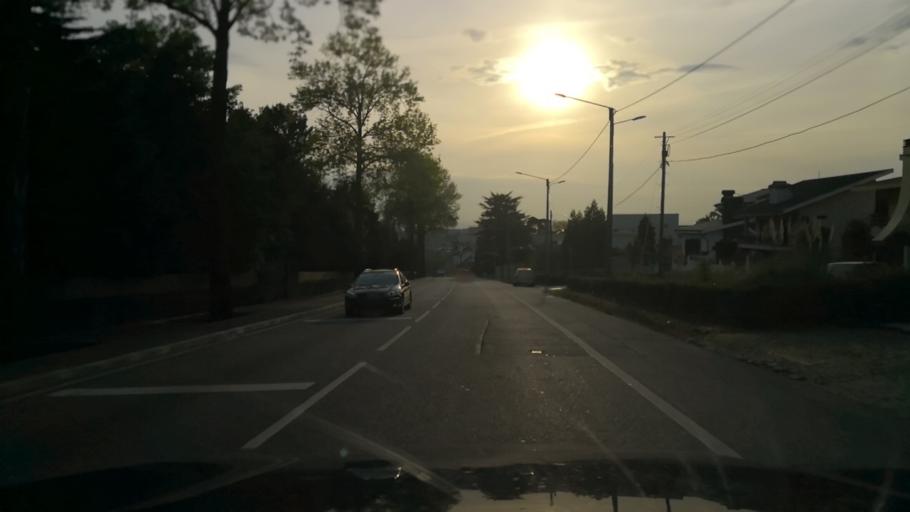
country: PT
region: Porto
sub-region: Gondomar
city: Baguim do Monte
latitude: 41.2068
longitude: -8.5360
